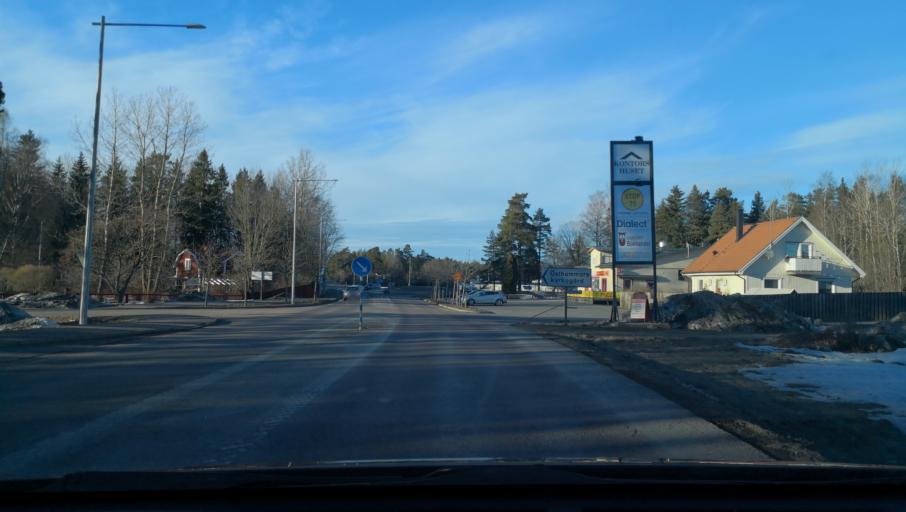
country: SE
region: Uppsala
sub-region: Osthammars Kommun
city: OEsthammar
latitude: 60.2535
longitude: 18.3468
